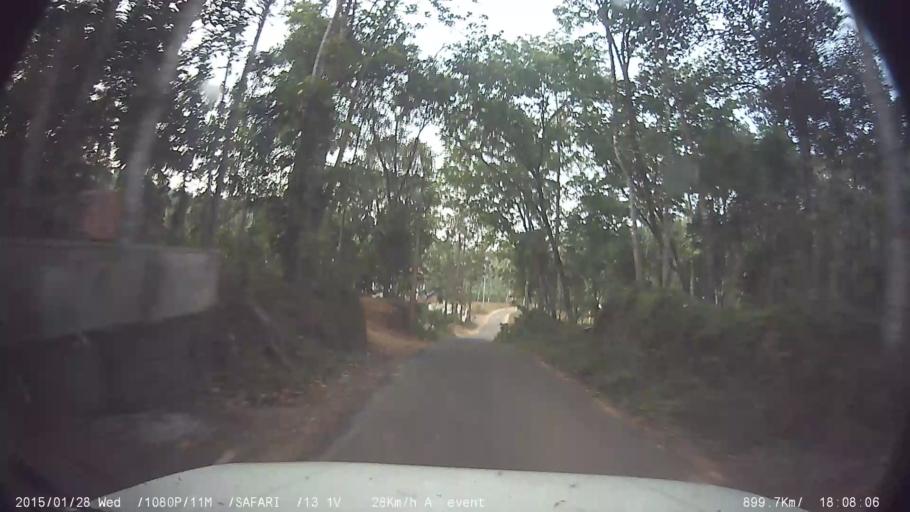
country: IN
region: Kerala
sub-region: Kottayam
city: Palackattumala
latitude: 9.7381
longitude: 76.5755
